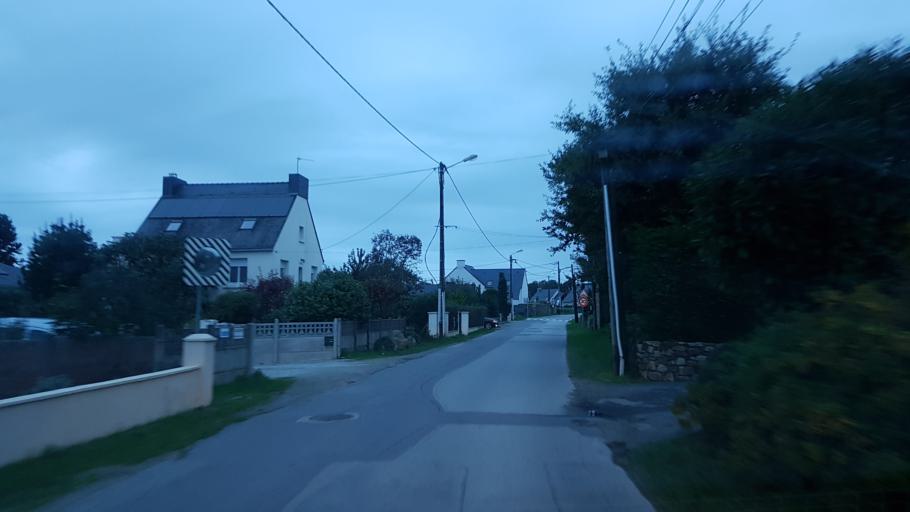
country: FR
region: Brittany
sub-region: Departement du Morbihan
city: Sarzeau
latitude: 47.5421
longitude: -2.7866
